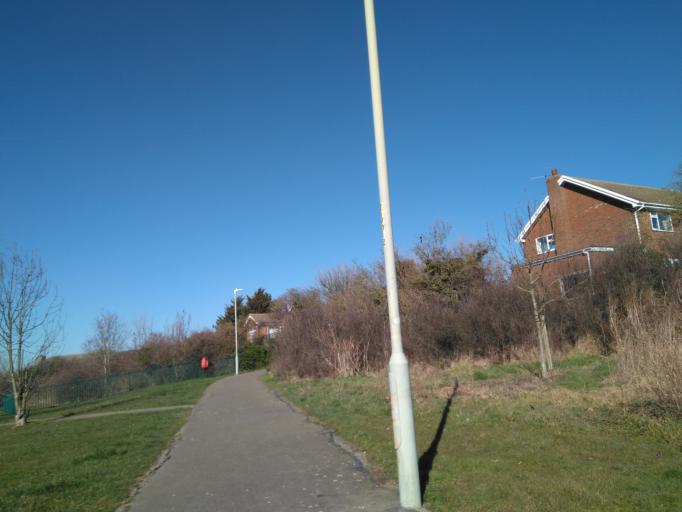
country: GB
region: England
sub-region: Kent
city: Whitstable
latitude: 51.3433
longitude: 1.0143
